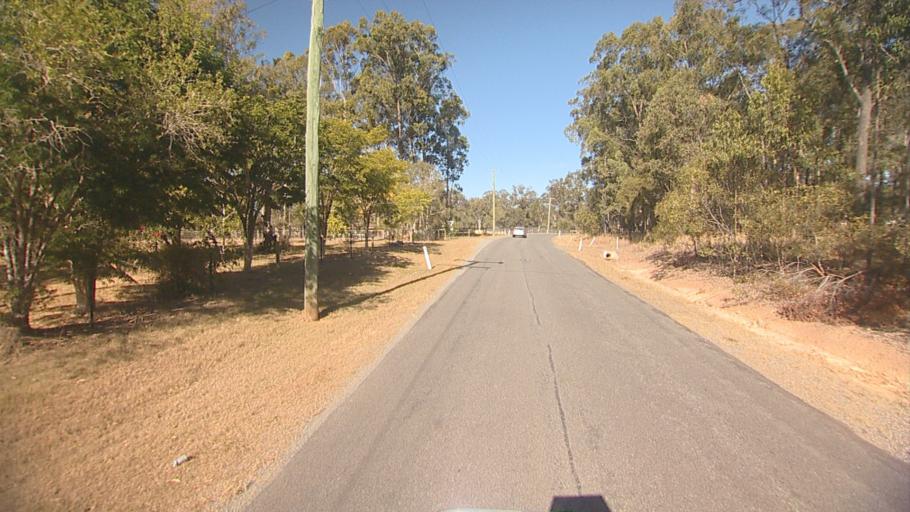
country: AU
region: Queensland
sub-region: Logan
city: Cedar Vale
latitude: -27.8540
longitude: 152.9934
